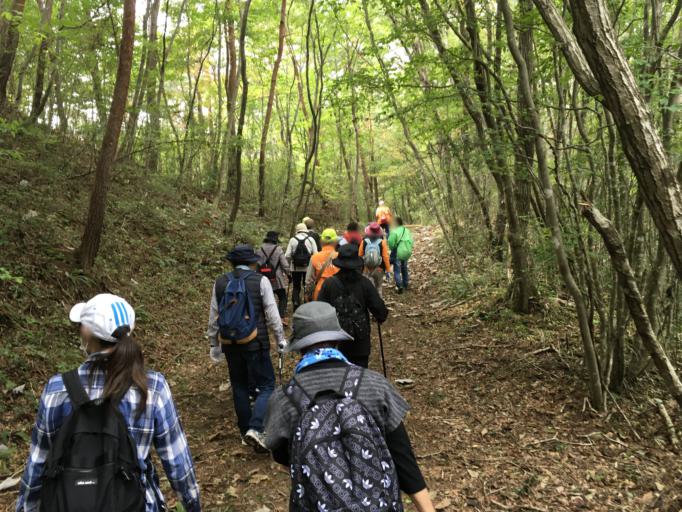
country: JP
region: Iwate
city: Ichinoseki
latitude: 38.8833
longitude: 141.0838
